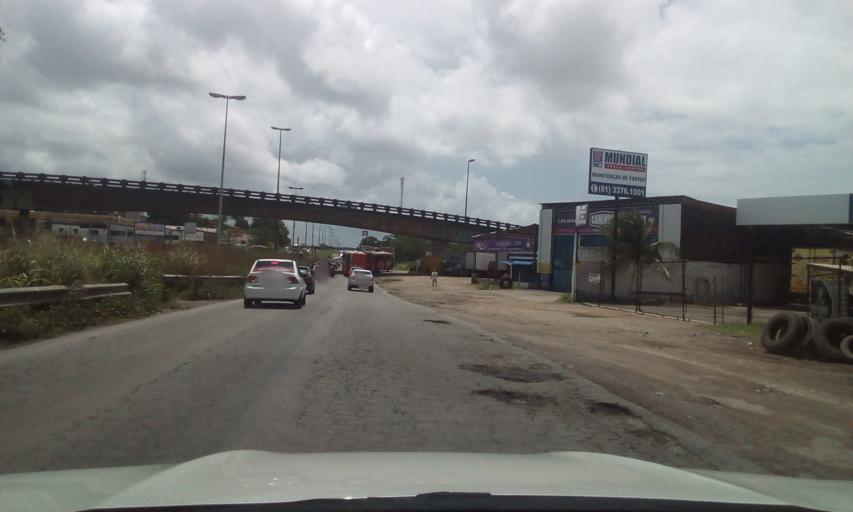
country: BR
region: Pernambuco
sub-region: Recife
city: Recife
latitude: -8.0818
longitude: -34.9432
